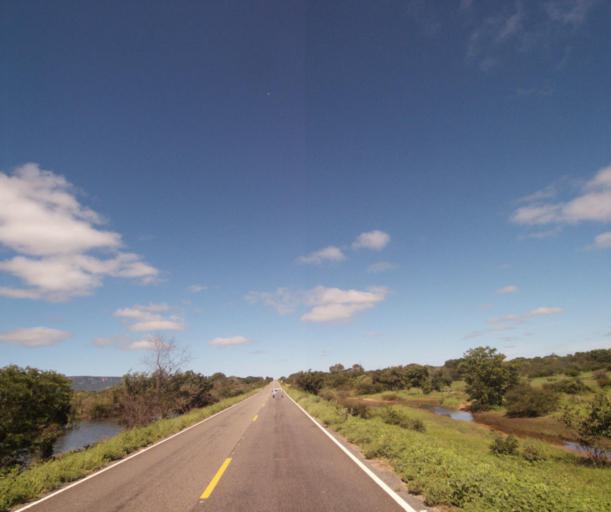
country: BR
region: Bahia
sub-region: Palmas De Monte Alto
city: Palmas de Monte Alto
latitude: -14.2398
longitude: -43.0411
